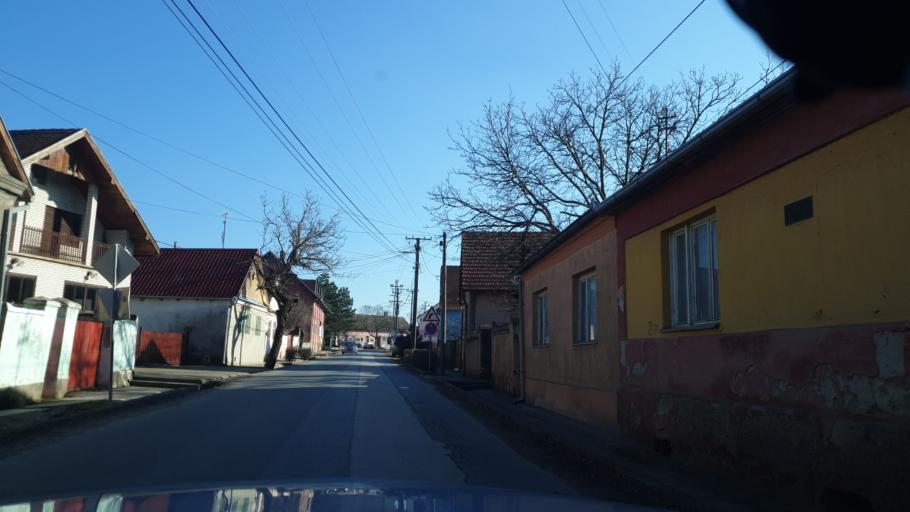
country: RS
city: Vrdnik
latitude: 45.1231
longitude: 19.7931
